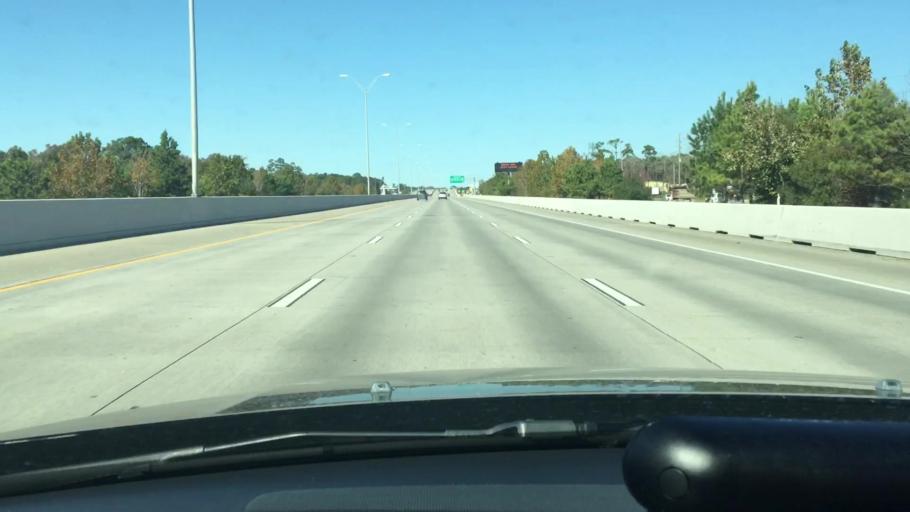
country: US
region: Texas
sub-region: Harris County
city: Sheldon
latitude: 29.8753
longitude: -95.1909
